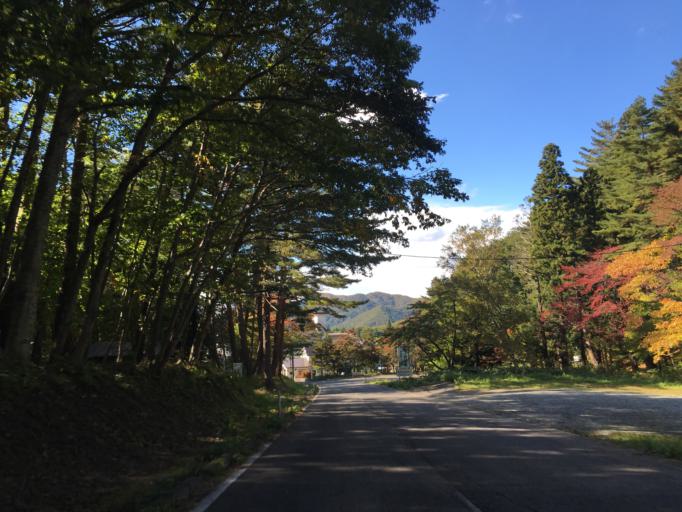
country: JP
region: Fukushima
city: Inawashiro
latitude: 37.6136
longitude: 140.2134
